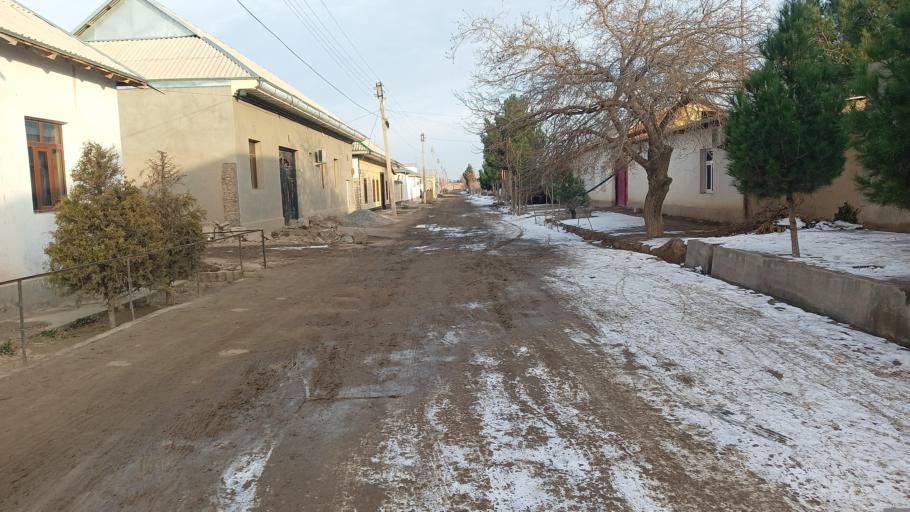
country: UZ
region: Qashqadaryo
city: Yangi Mirishkor
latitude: 38.8926
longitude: 65.3052
